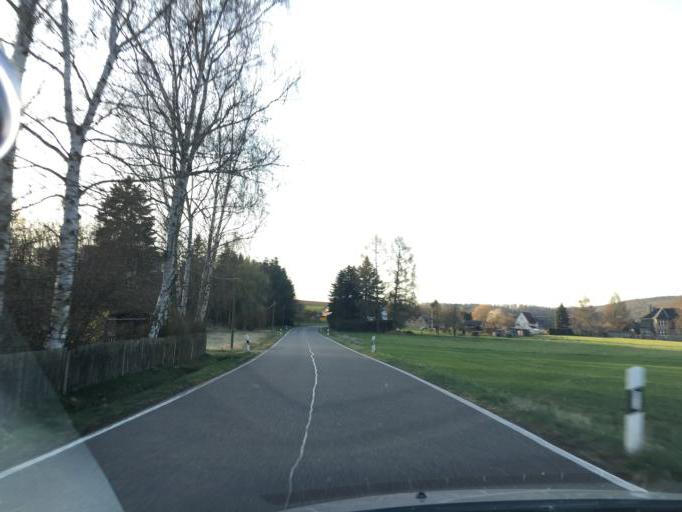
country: DE
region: Saxony
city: Wechselburg
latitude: 50.9918
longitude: 12.7724
